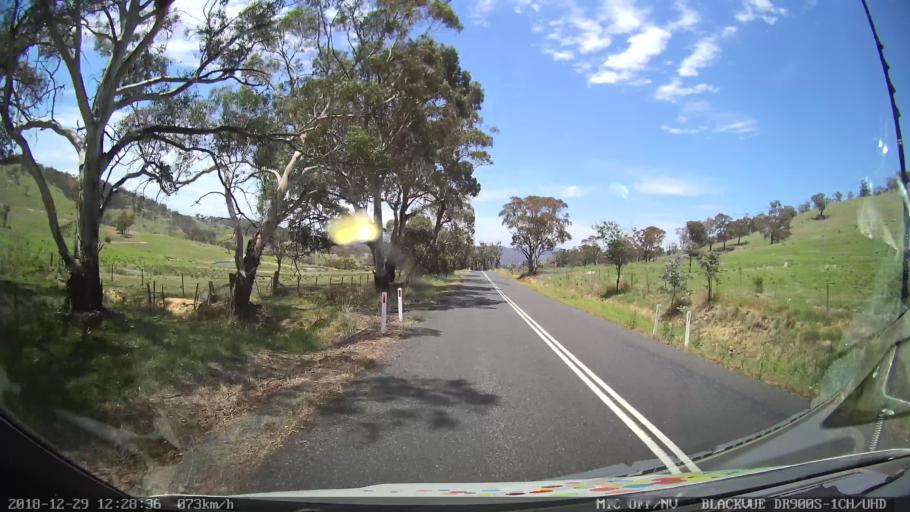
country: AU
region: Australian Capital Territory
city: Macarthur
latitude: -35.4883
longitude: 149.2266
